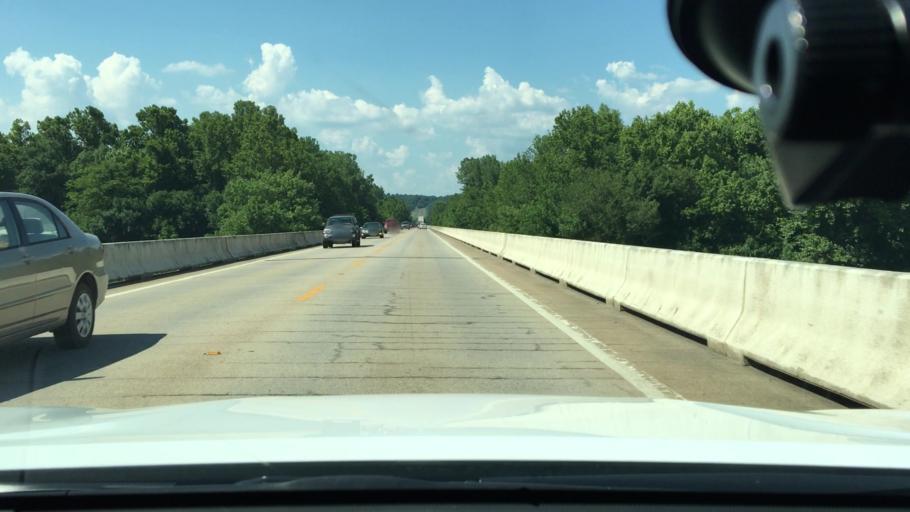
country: US
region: Arkansas
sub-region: Johnson County
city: Clarksville
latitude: 35.3954
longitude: -93.5306
